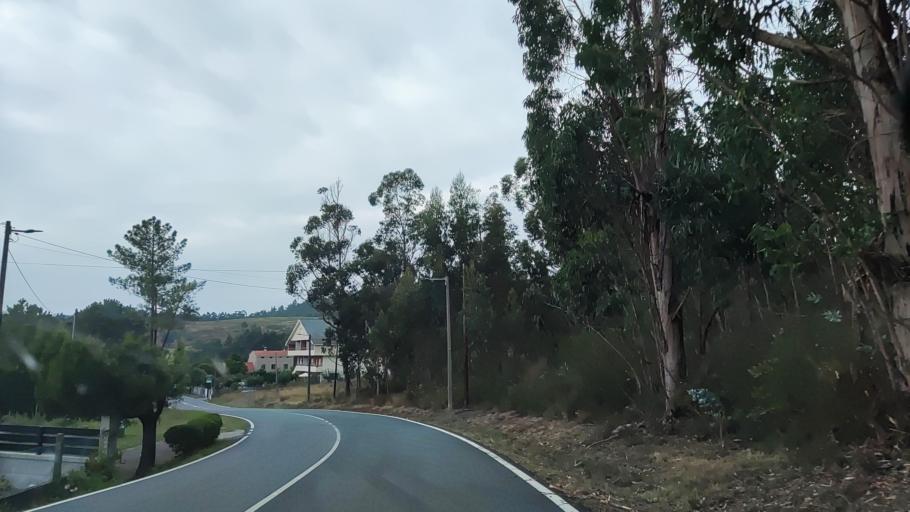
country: ES
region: Galicia
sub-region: Provincia de Pontevedra
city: Catoira
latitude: 42.6524
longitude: -8.7589
